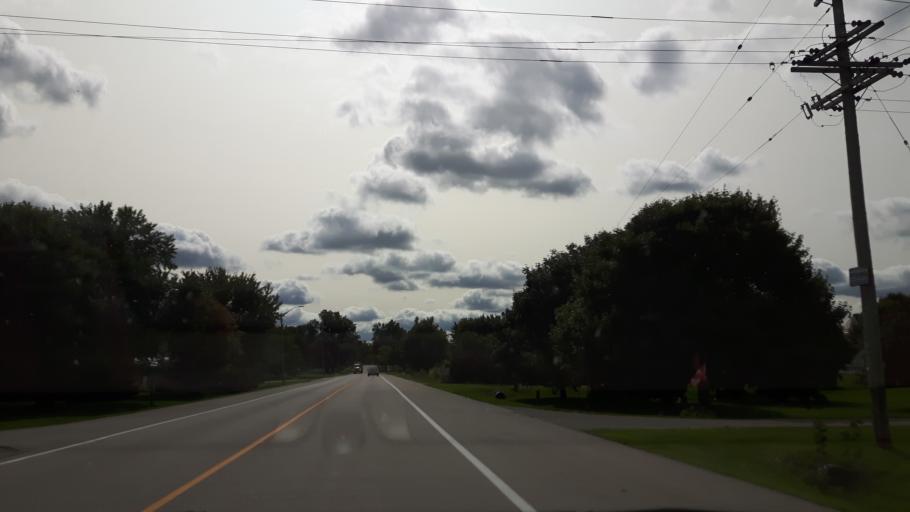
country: CA
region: Ontario
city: Huron East
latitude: 43.5616
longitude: -81.3865
